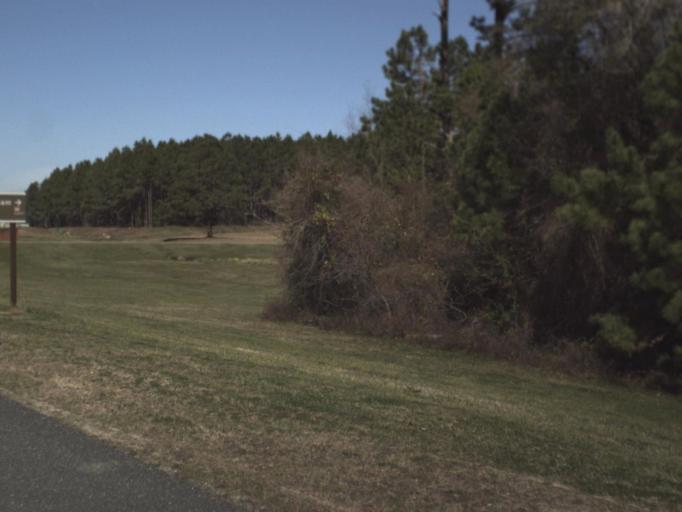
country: US
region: Florida
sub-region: Gadsden County
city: Chattahoochee
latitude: 30.6990
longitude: -84.8733
